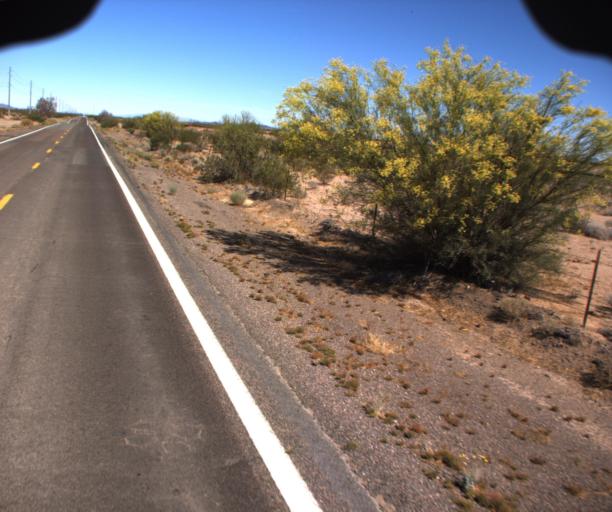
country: US
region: Arizona
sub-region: La Paz County
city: Salome
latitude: 33.8114
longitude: -113.8493
